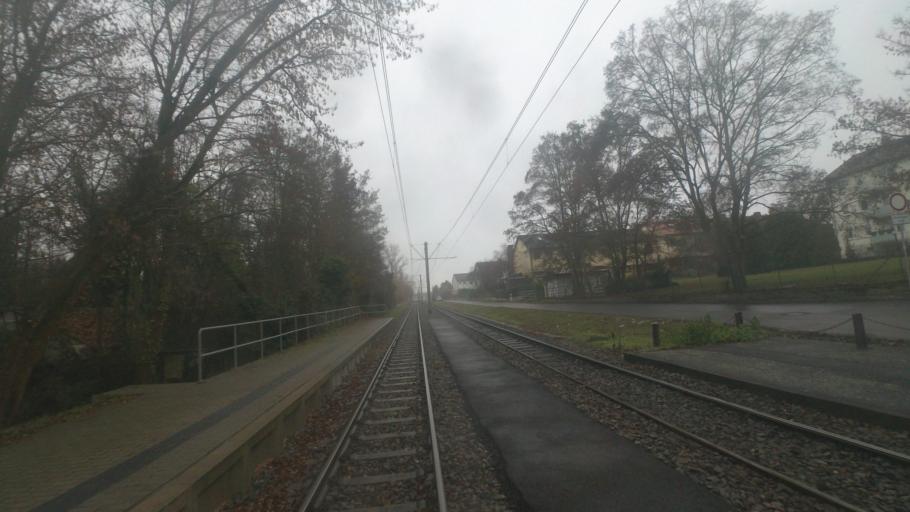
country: DE
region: Rheinland-Pfalz
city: Maxdorf
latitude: 49.4762
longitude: 8.2892
